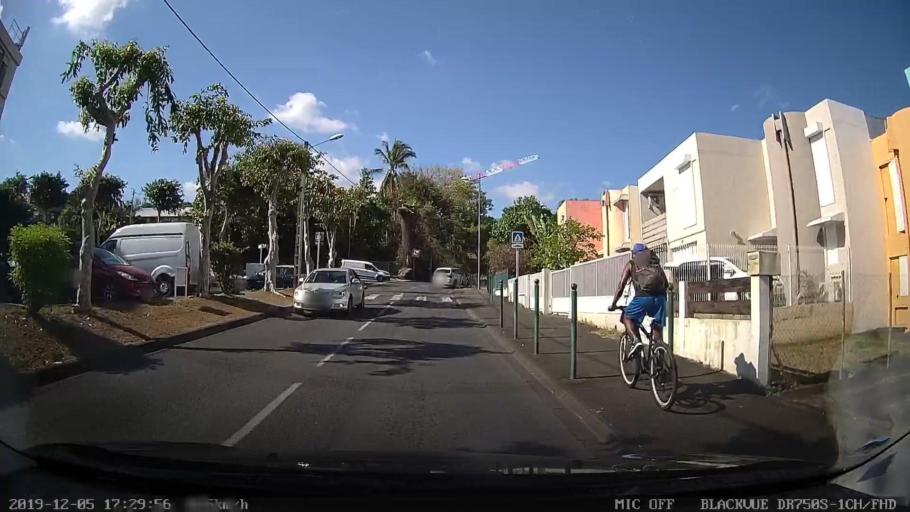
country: RE
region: Reunion
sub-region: Reunion
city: Saint-Denis
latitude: -20.8982
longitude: 55.4803
